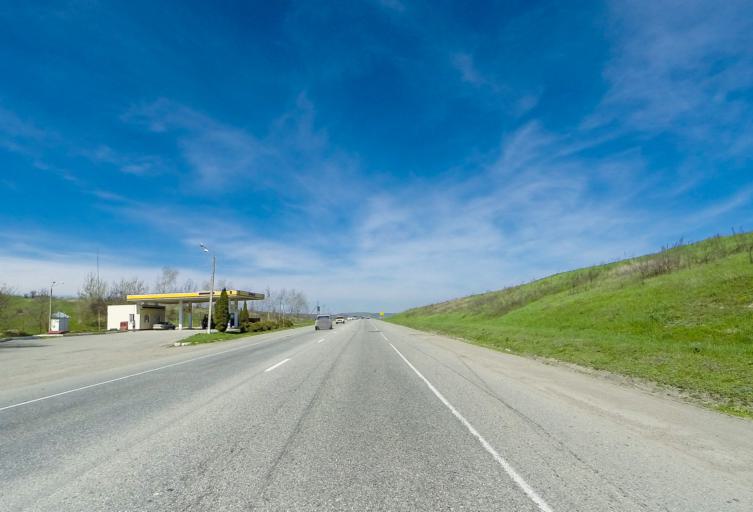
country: RU
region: Kabardino-Balkariya
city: Dugulubgey
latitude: 43.6416
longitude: 43.5445
